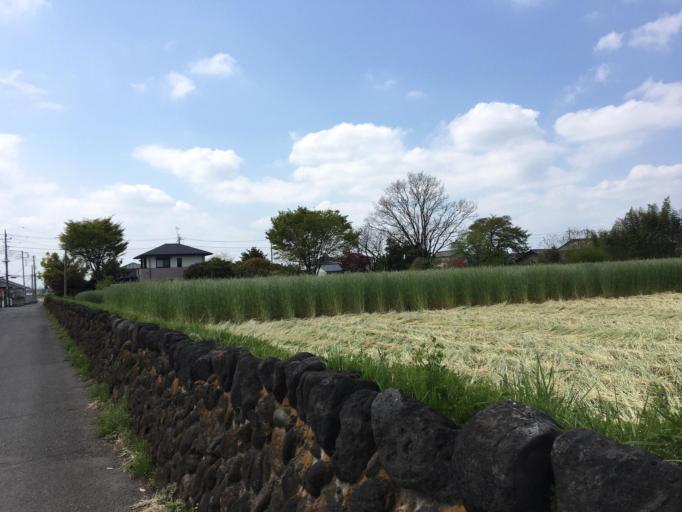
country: JP
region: Gunma
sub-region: Sawa-gun
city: Tamamura
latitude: 36.2859
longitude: 139.1604
